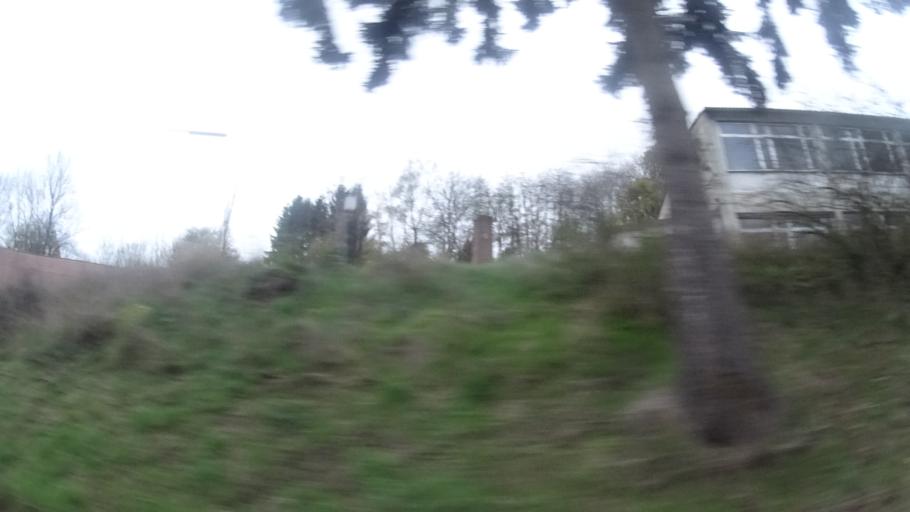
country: DE
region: Hesse
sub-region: Regierungsbezirk Giessen
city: Freiensteinau
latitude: 50.3964
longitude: 9.4280
